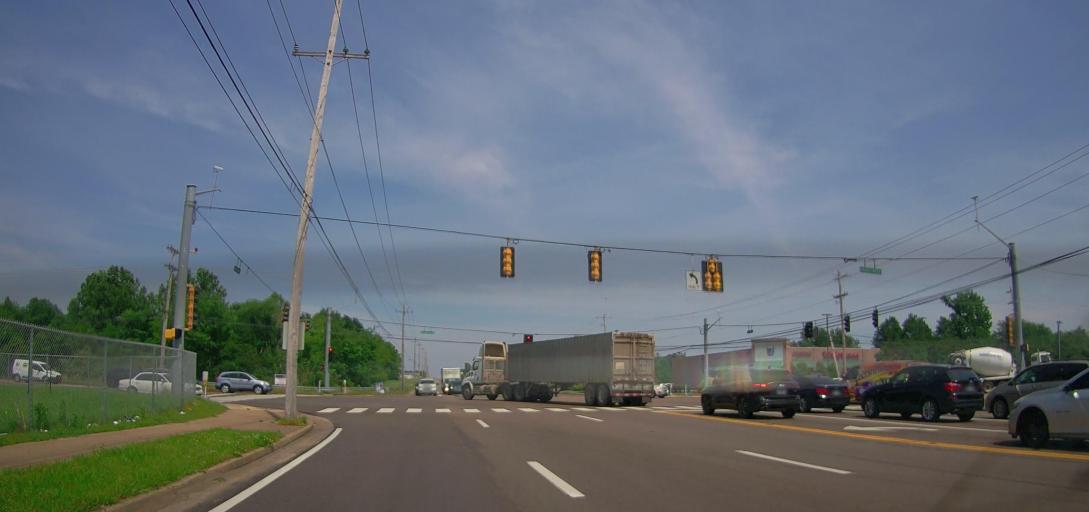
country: US
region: Mississippi
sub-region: De Soto County
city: Olive Branch
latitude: 35.0206
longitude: -89.7964
